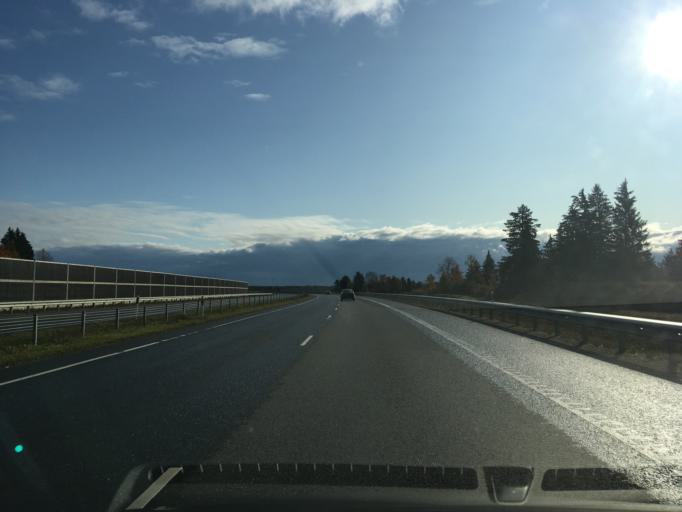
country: EE
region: Harju
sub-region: Rae vald
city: Vaida
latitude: 59.1848
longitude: 25.0716
